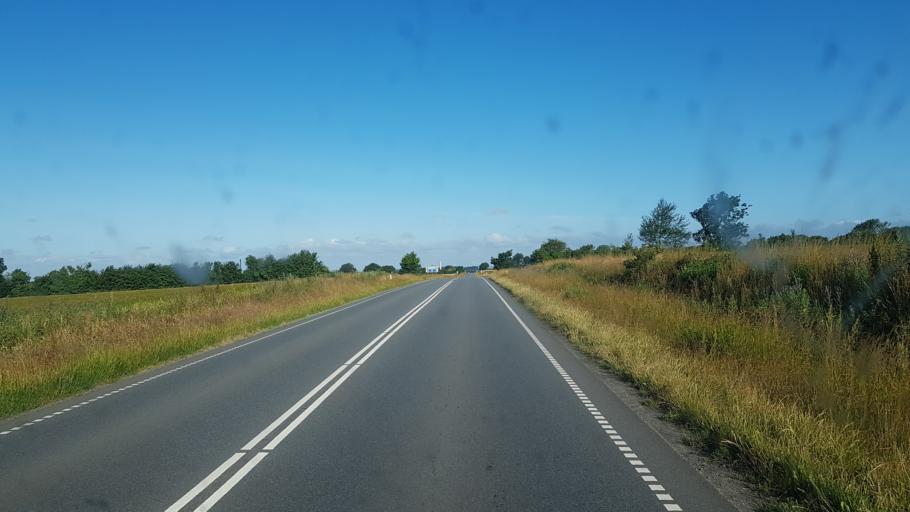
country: DK
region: South Denmark
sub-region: Vejen Kommune
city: Rodding
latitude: 55.3733
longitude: 9.0764
